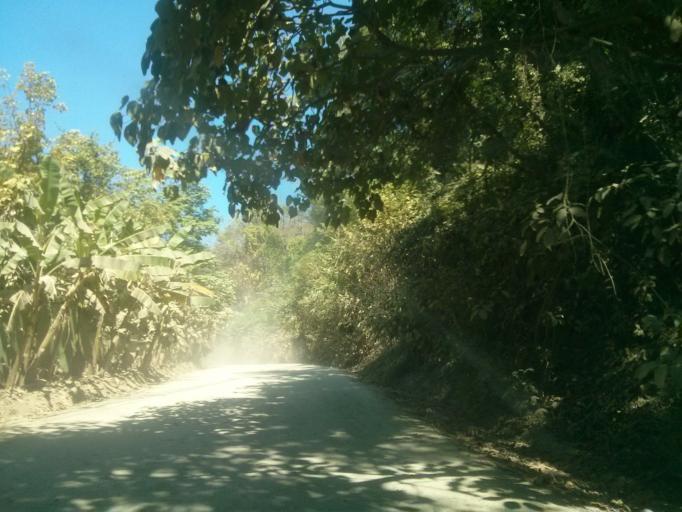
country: CR
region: Guanacaste
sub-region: Canton de Nandayure
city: Bejuco
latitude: 9.6602
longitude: -85.1852
